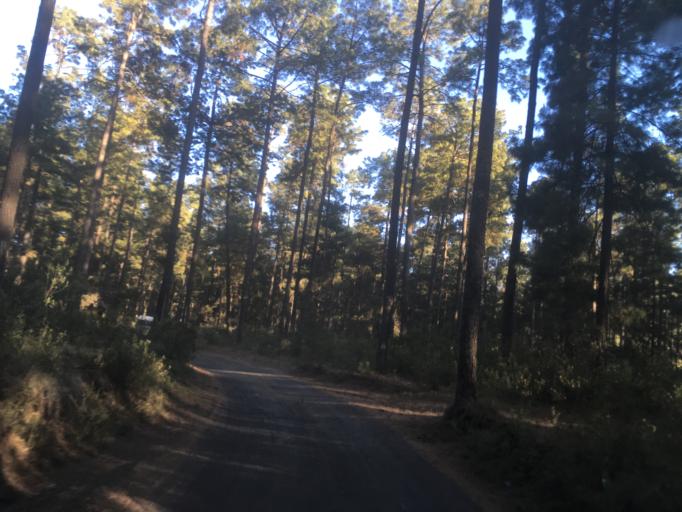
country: MX
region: Michoacan
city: Angahuan
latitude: 19.4619
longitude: -102.2130
